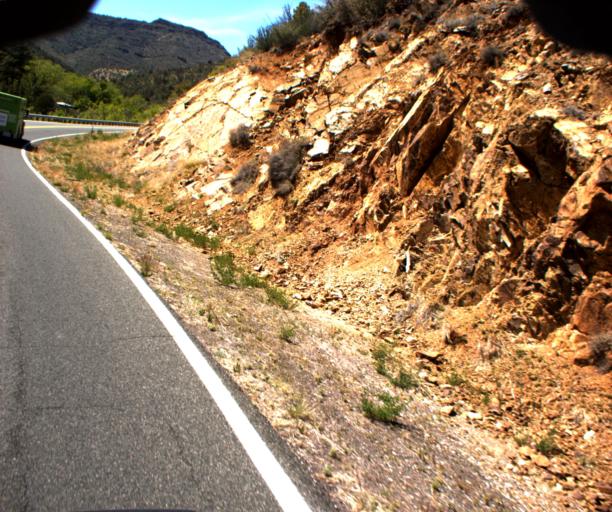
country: US
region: Arizona
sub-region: Yavapai County
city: Clarkdale
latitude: 34.7391
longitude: -112.1310
